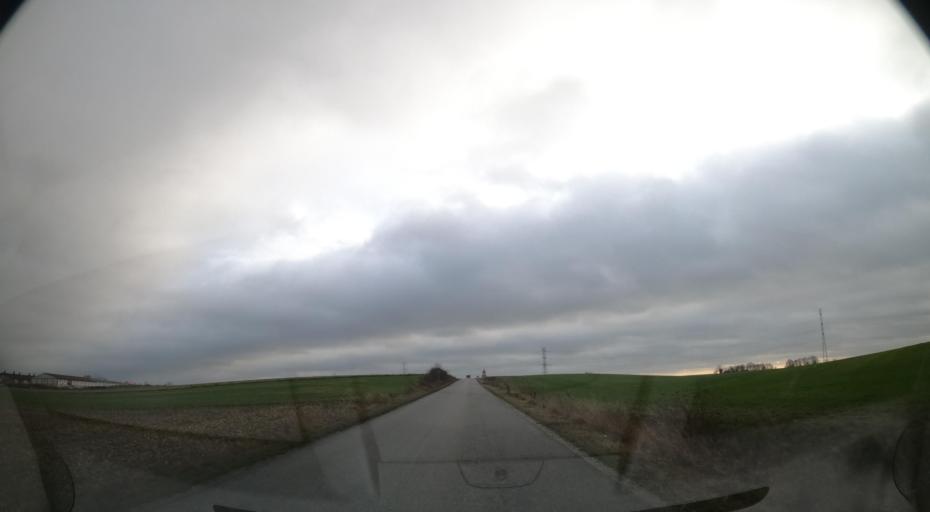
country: PL
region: Kujawsko-Pomorskie
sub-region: Powiat nakielski
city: Sadki
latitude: 53.1832
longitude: 17.4034
